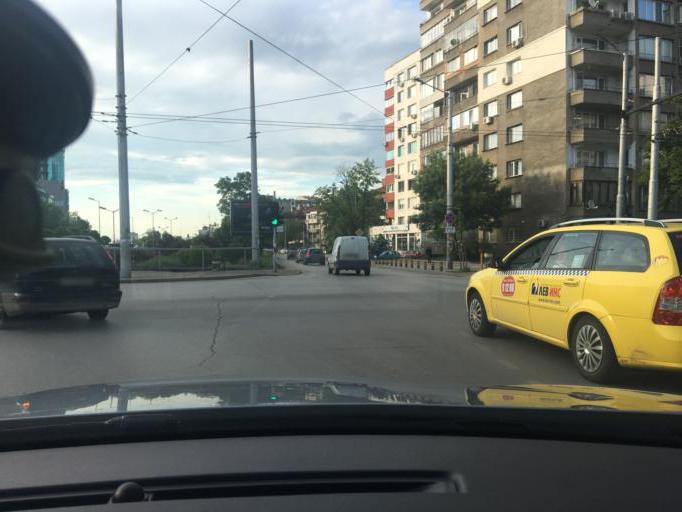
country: BG
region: Sofia-Capital
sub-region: Stolichna Obshtina
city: Sofia
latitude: 42.6843
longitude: 23.3012
